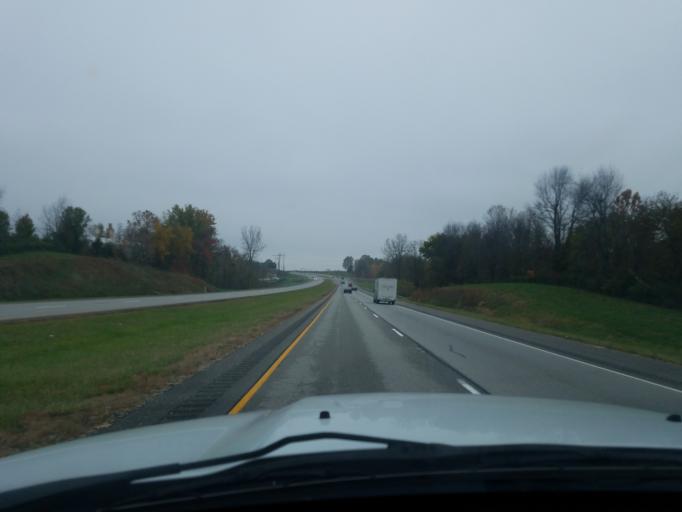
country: US
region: Kentucky
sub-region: Hardin County
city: Elizabethtown
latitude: 37.6616
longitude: -85.8377
